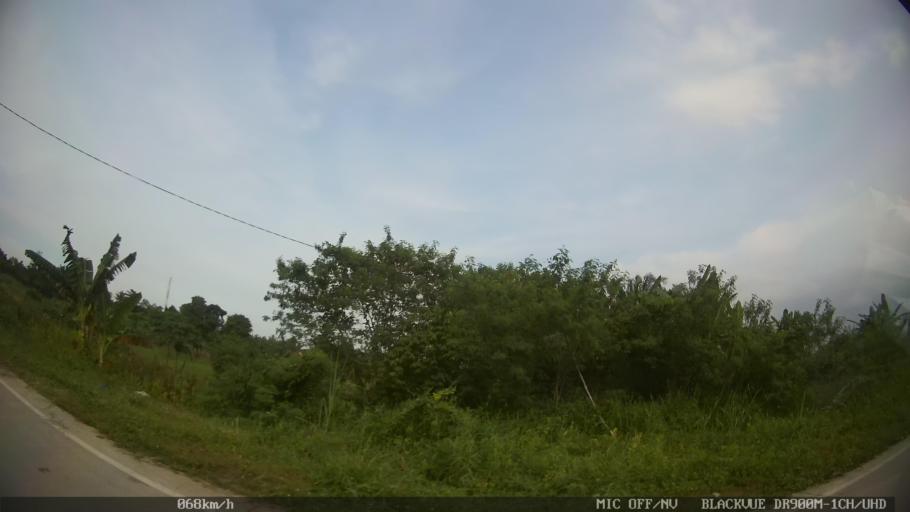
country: ID
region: North Sumatra
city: Binjai
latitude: 3.5990
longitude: 98.5330
